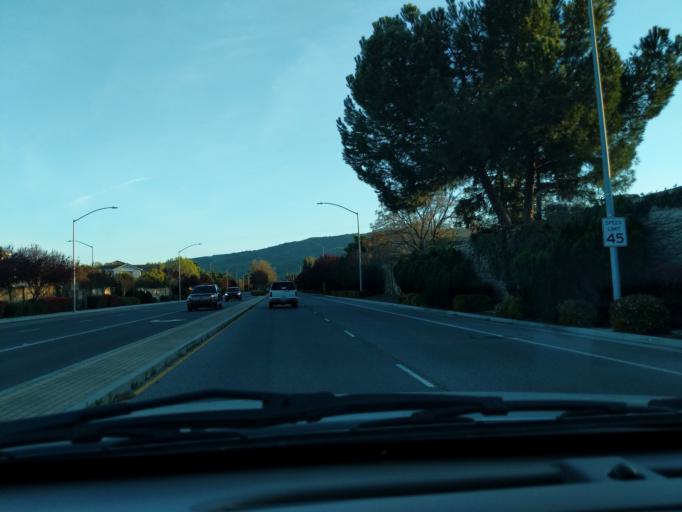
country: US
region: California
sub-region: Santa Clara County
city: Gilroy
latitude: 37.0275
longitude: -121.5983
